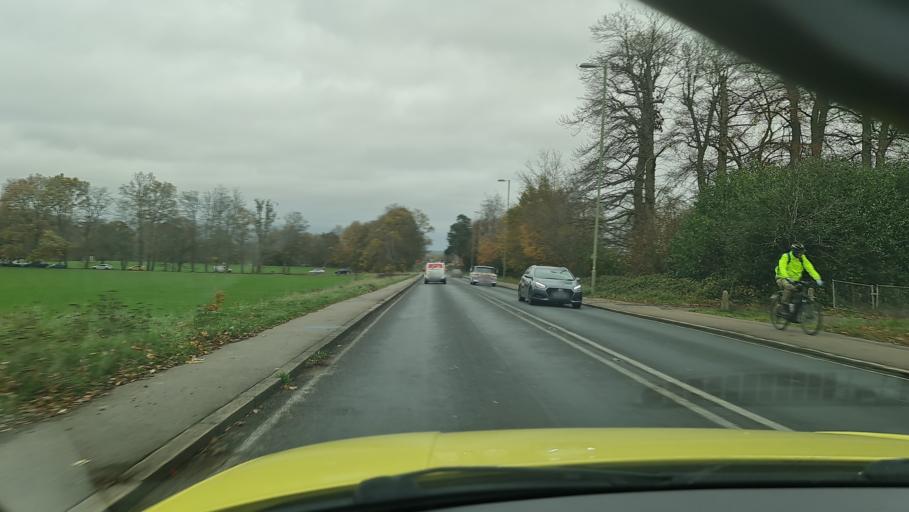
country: GB
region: England
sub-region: Hampshire
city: Aldershot
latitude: 51.2541
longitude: -0.7743
